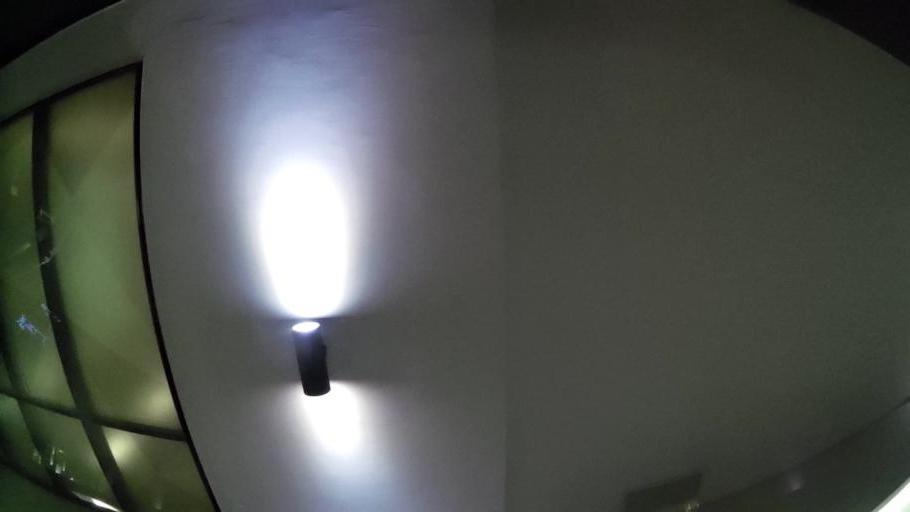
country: PA
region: Panama
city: Panama
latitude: 8.9875
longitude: -79.5202
